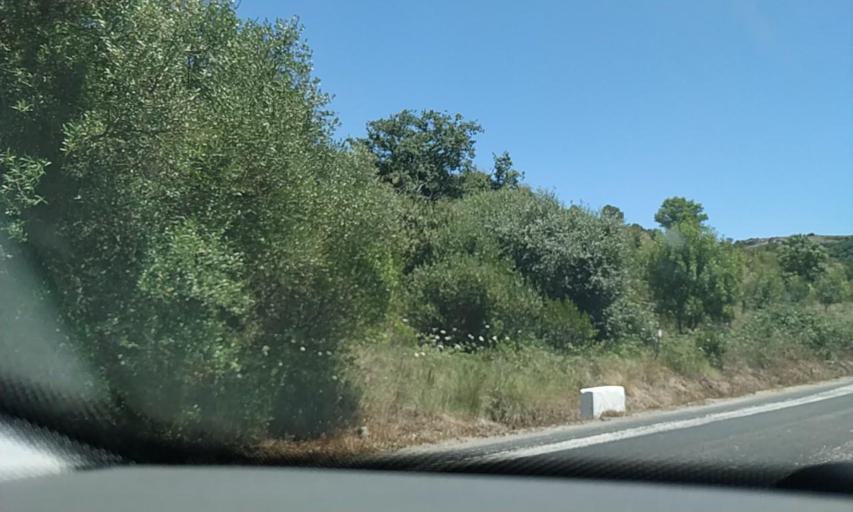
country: PT
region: Lisbon
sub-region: Sintra
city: Almargem
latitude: 38.8694
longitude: -9.2284
